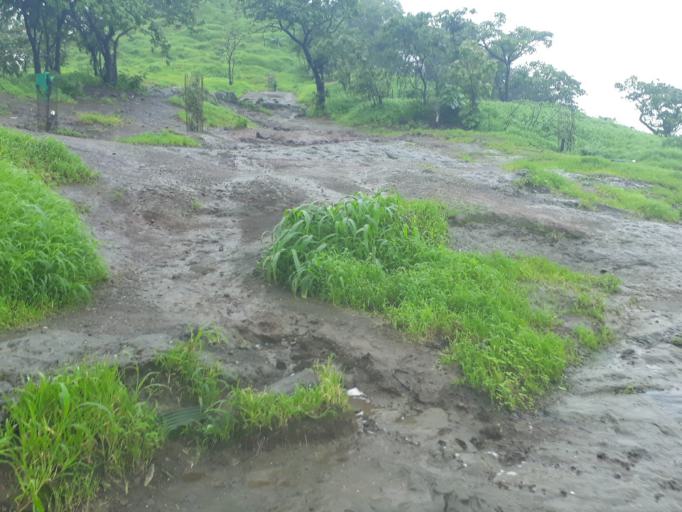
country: IN
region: Maharashtra
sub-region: Pune Division
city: Lonavla
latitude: 18.6317
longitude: 73.5155
